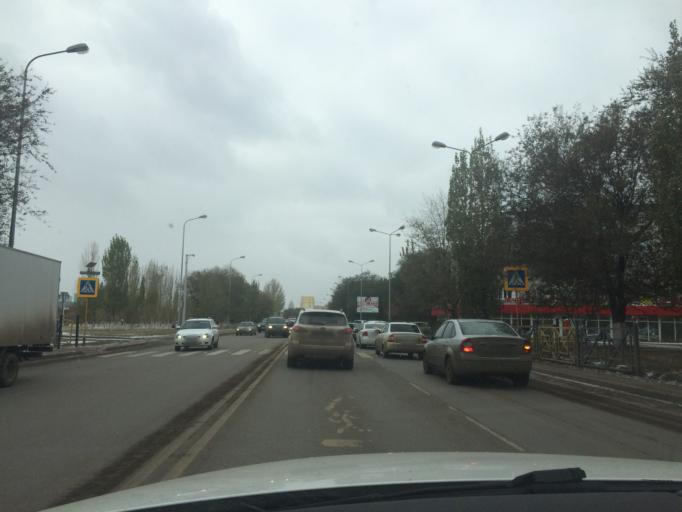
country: KZ
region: Astana Qalasy
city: Astana
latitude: 51.1570
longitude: 71.4583
